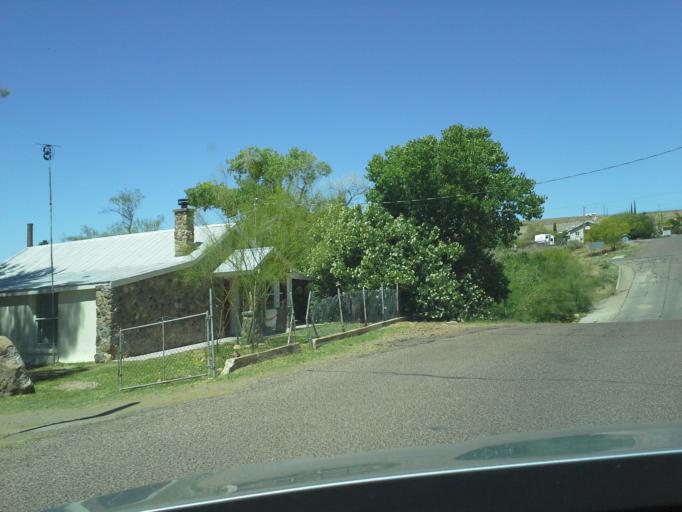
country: US
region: Arizona
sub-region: Pinal County
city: Superior
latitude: 33.2922
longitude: -111.1007
